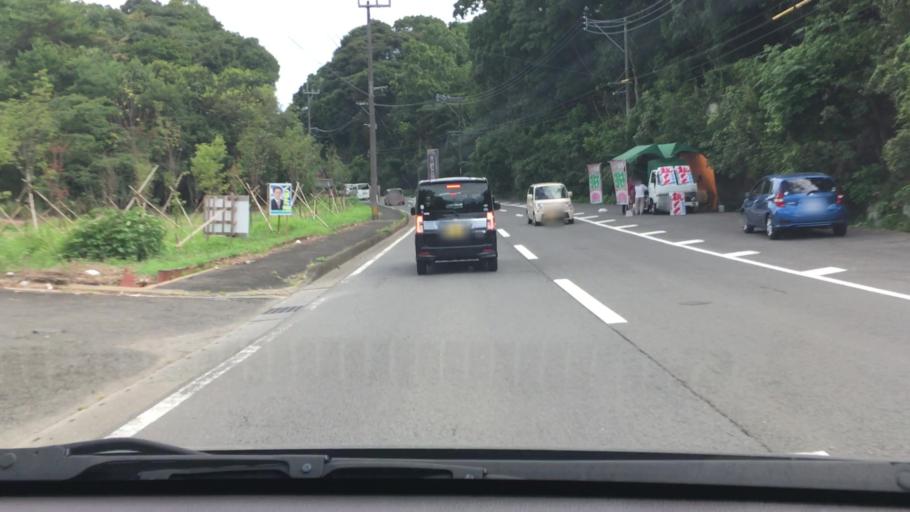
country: JP
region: Nagasaki
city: Togitsu
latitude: 32.9263
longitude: 129.7865
